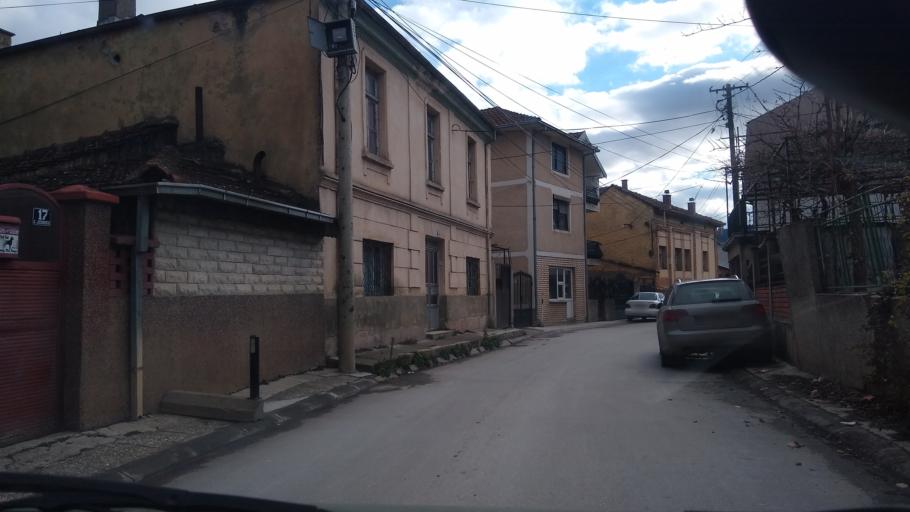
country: MK
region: Bitola
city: Bitola
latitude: 41.0274
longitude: 21.3310
